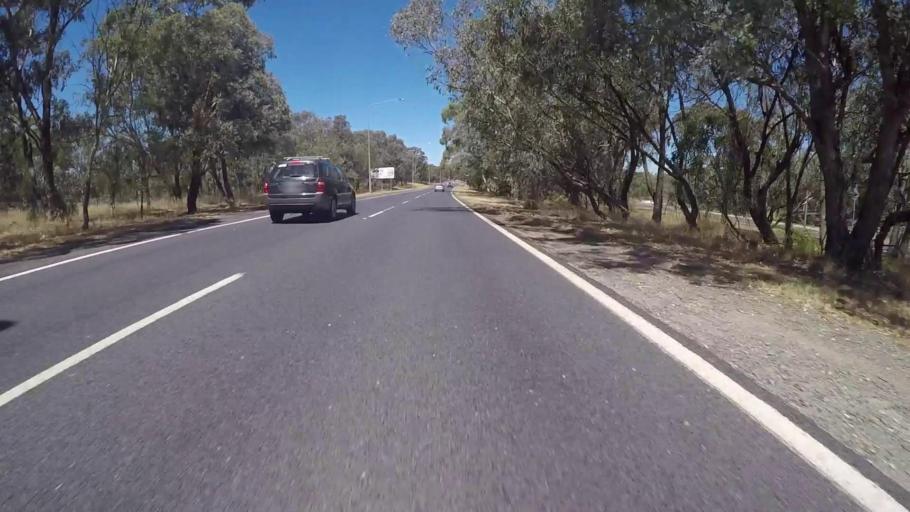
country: AU
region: Australian Capital Territory
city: Forrest
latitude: -35.3459
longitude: 149.0691
